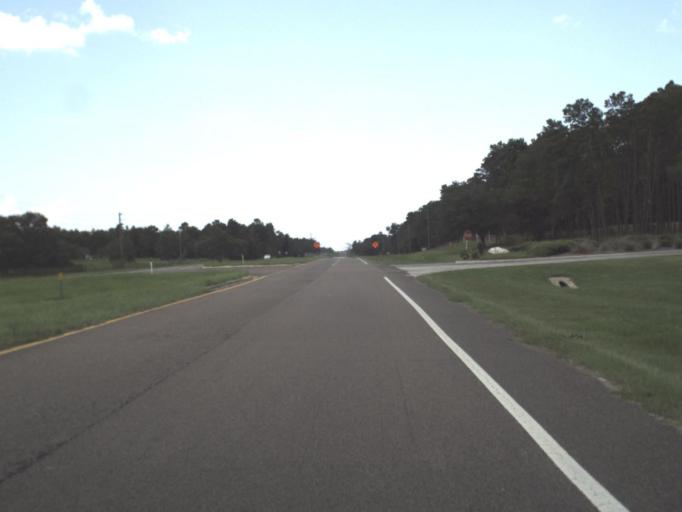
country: US
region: Florida
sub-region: Citrus County
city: Sugarmill Woods
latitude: 28.6767
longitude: -82.4843
